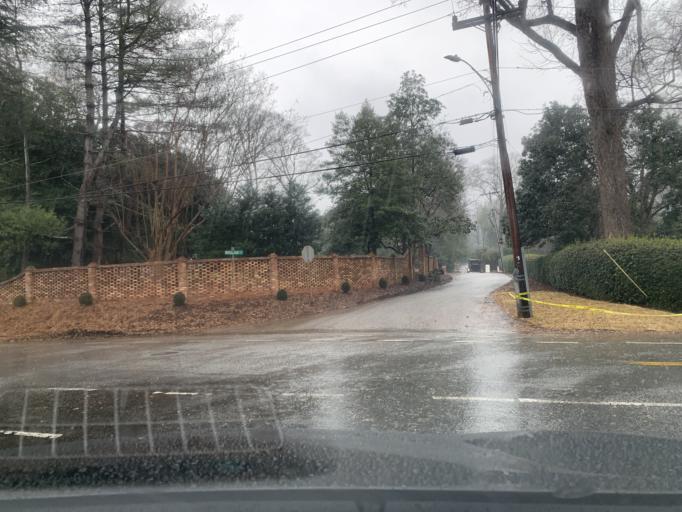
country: US
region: South Carolina
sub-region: Greenville County
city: Greenville
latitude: 34.8394
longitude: -82.3899
